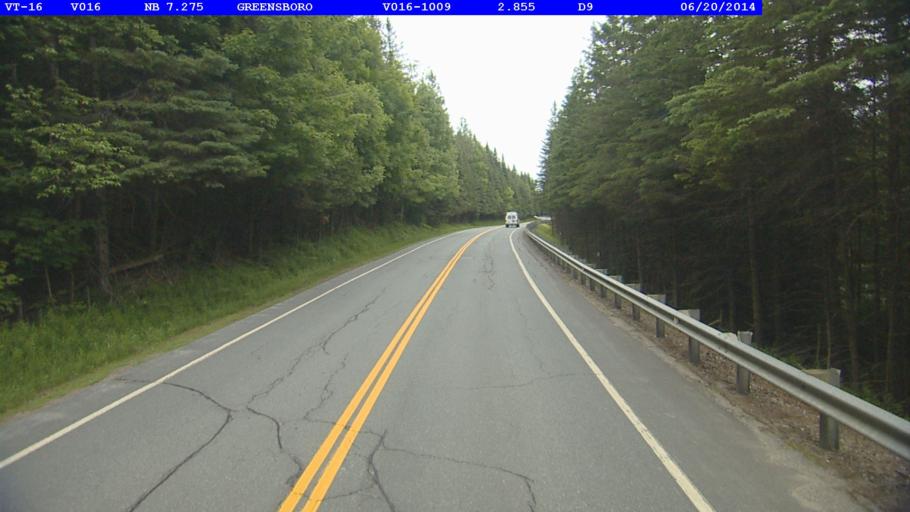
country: US
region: Vermont
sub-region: Caledonia County
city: Hardwick
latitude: 44.5806
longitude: -72.2418
